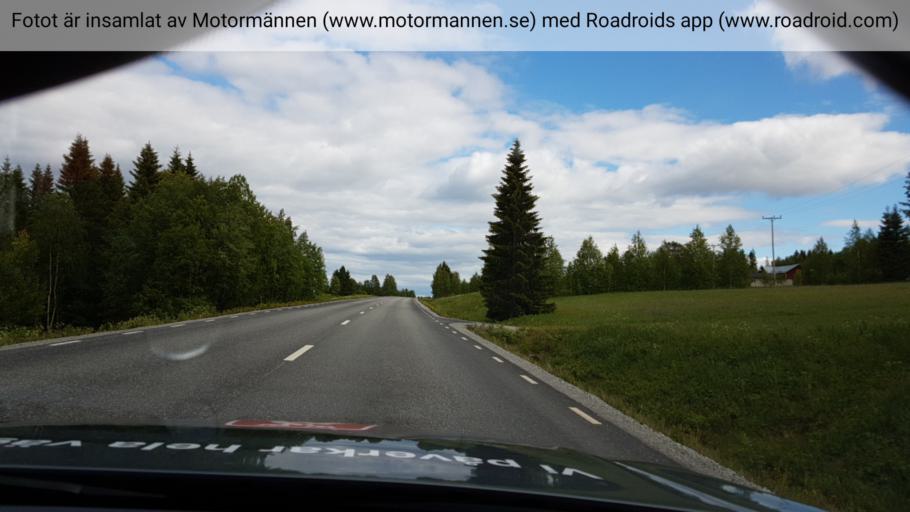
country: SE
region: Jaemtland
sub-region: Stroemsunds Kommun
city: Stroemsund
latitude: 64.2197
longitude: 15.5445
